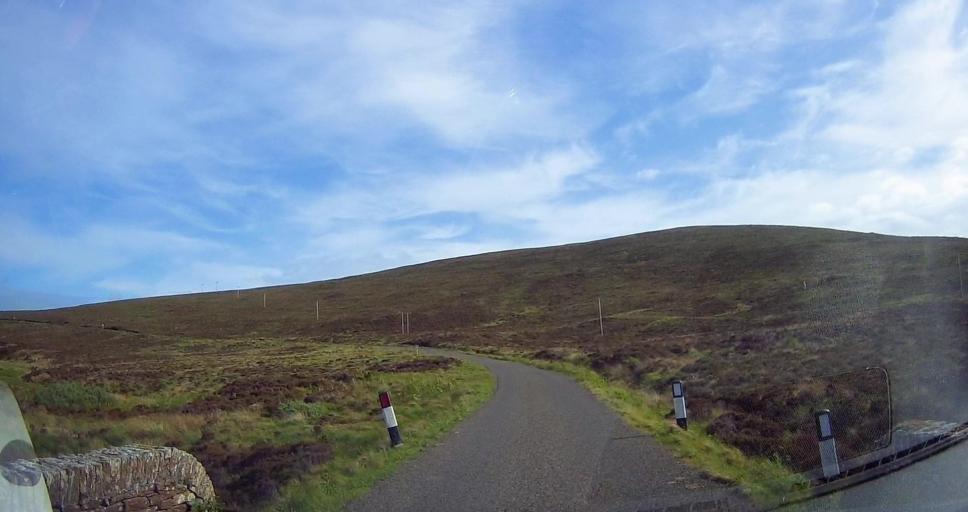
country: GB
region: Scotland
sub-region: Orkney Islands
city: Stromness
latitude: 58.8702
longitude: -3.2319
